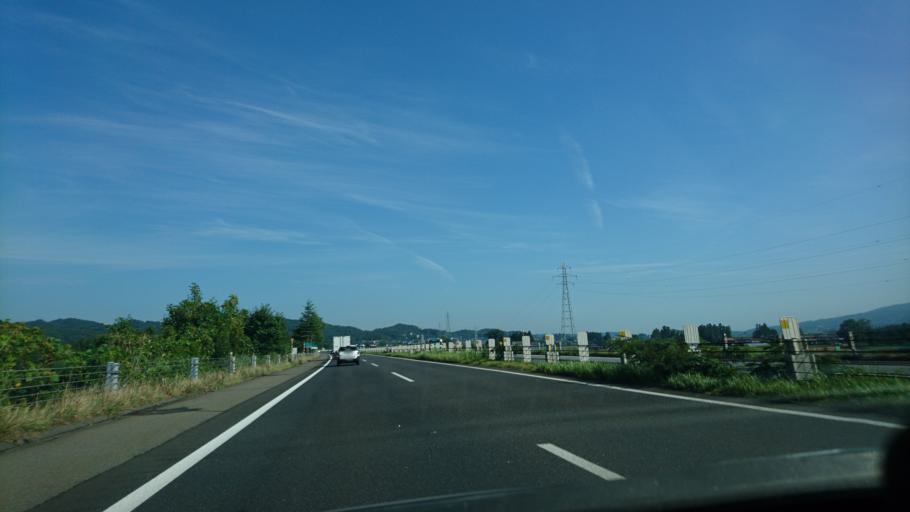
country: JP
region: Iwate
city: Ichinoseki
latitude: 38.9735
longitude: 141.1119
